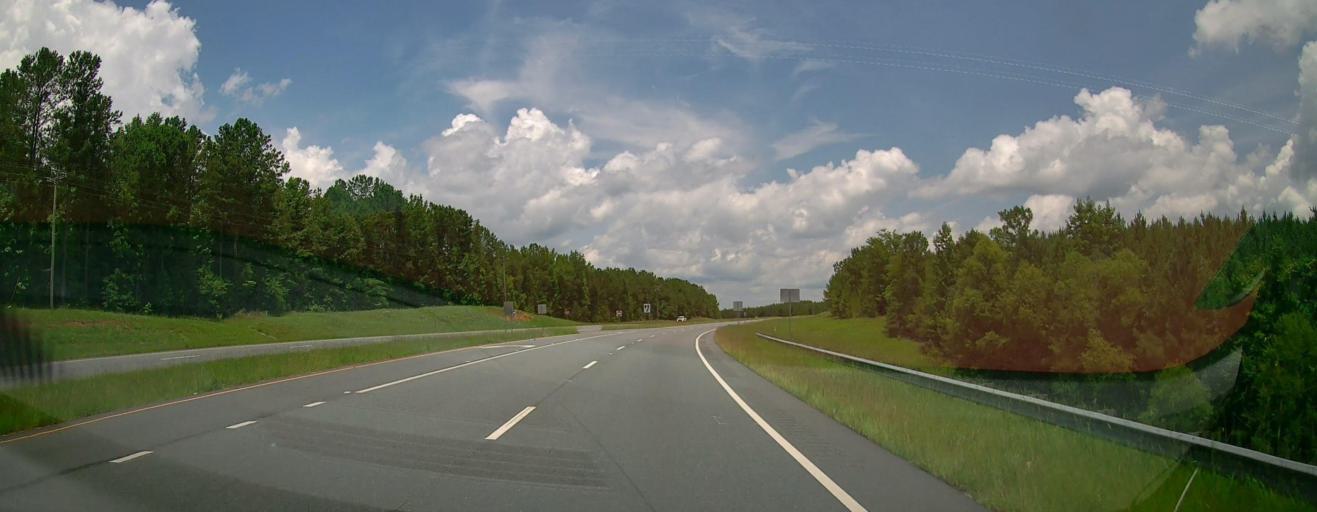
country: US
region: Georgia
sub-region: Upson County
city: Thomaston
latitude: 32.7738
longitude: -84.2483
